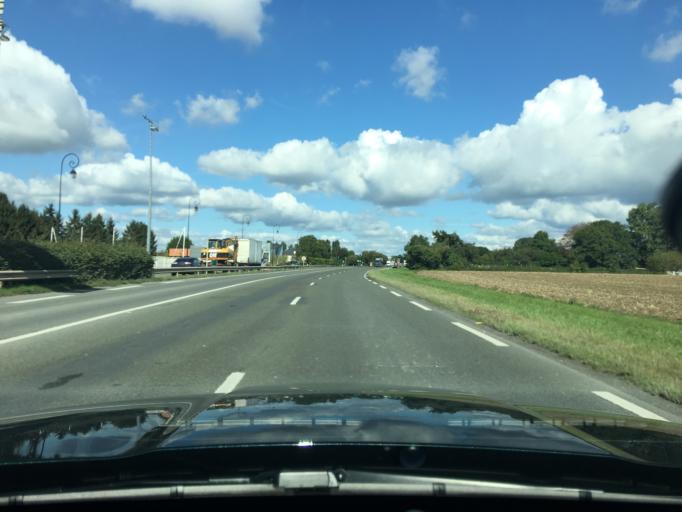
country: FR
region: Ile-de-France
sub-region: Departement du Val-d'Oise
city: Louvres
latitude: 49.0481
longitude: 2.5120
